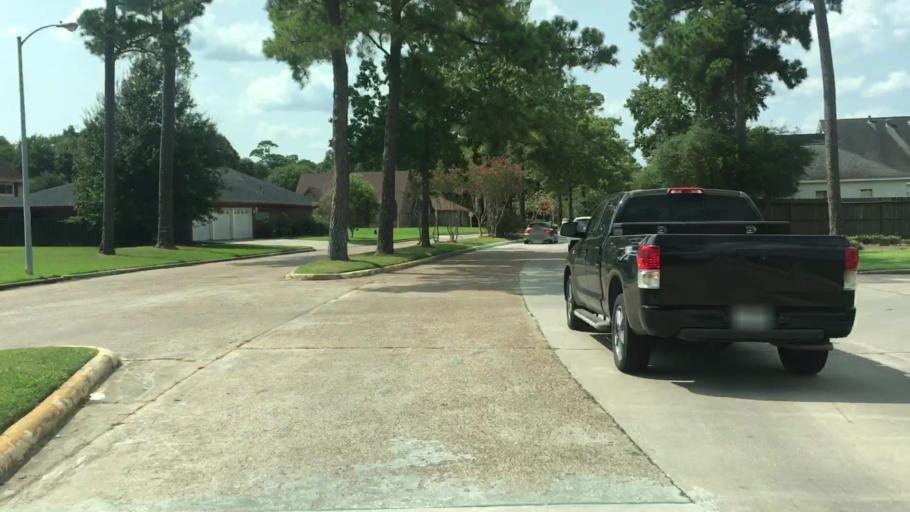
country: US
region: Texas
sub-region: Harris County
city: Atascocita
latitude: 30.0040
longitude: -95.1549
